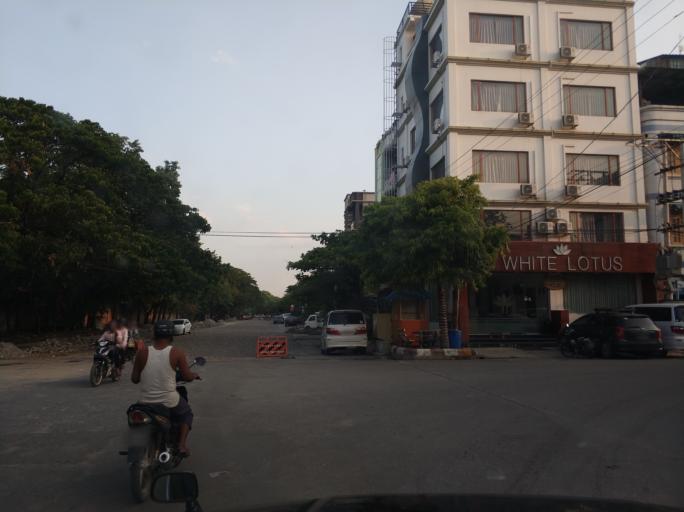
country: MM
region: Mandalay
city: Mandalay
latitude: 21.9740
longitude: 96.0850
